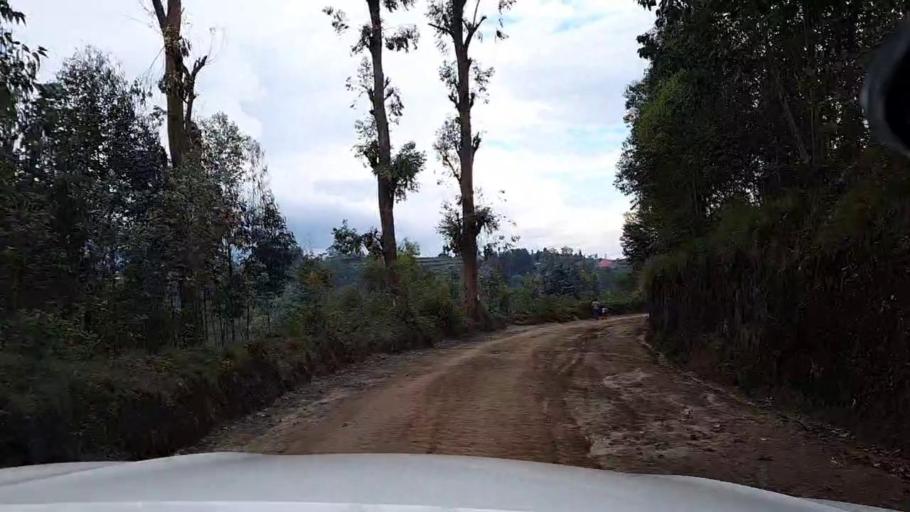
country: BI
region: Kayanza
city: Kayanza
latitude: -2.7975
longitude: 29.5003
